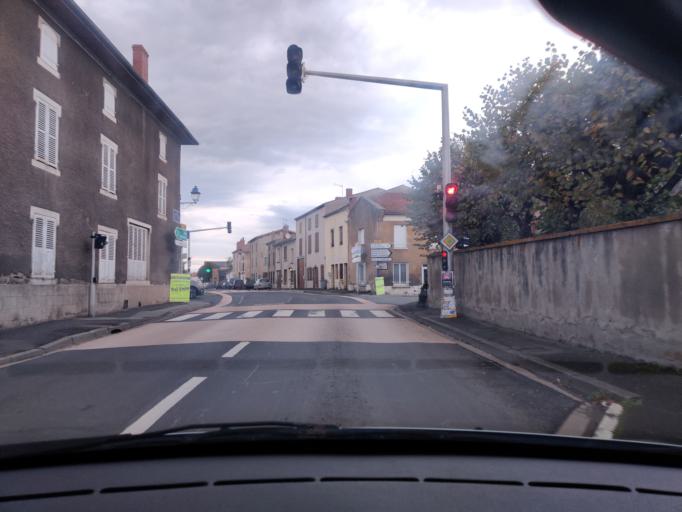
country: FR
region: Auvergne
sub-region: Departement du Puy-de-Dome
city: Combronde
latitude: 45.9825
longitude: 3.0881
